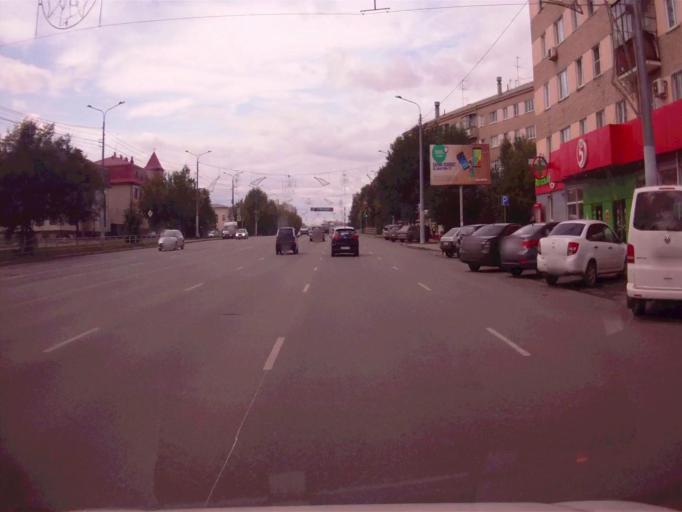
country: RU
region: Chelyabinsk
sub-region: Gorod Chelyabinsk
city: Chelyabinsk
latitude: 55.1391
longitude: 61.3990
